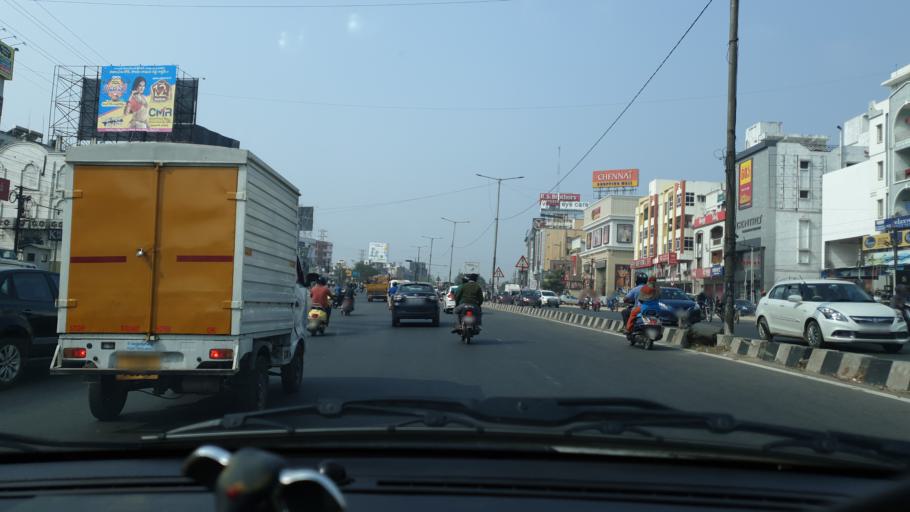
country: IN
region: Telangana
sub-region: Medak
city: Serilingampalle
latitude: 17.4955
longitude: 78.3340
